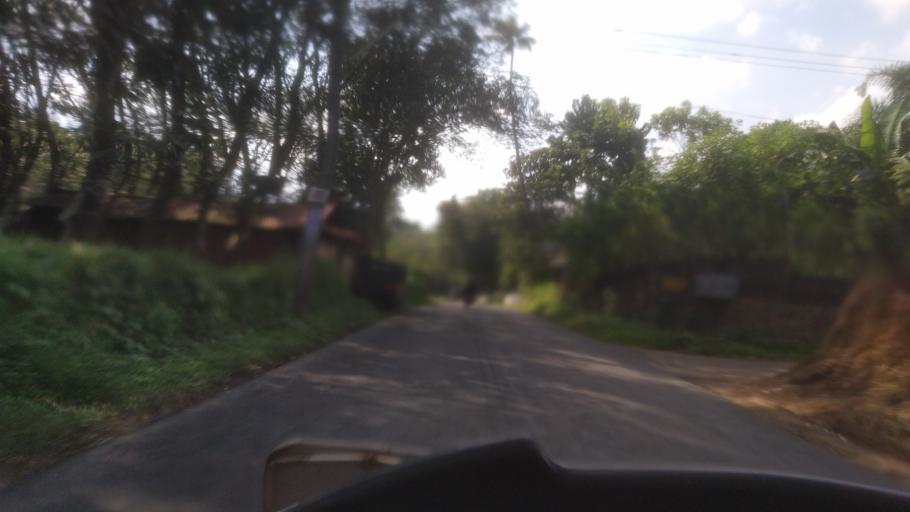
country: IN
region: Kerala
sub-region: Ernakulam
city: Kotamangalam
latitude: 10.0020
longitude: 76.7324
